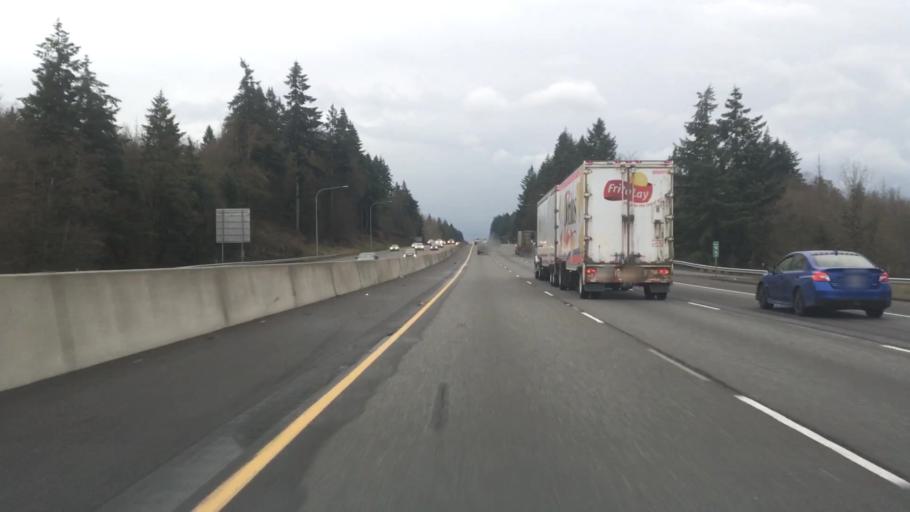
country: US
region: Washington
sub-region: Thurston County
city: Tenino
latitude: 46.8937
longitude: -122.9617
